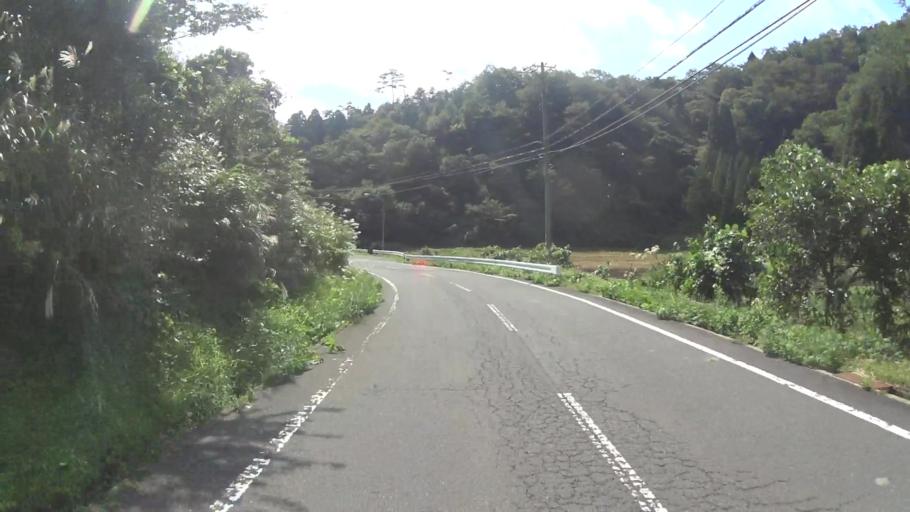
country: JP
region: Kyoto
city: Miyazu
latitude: 35.6952
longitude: 135.1707
